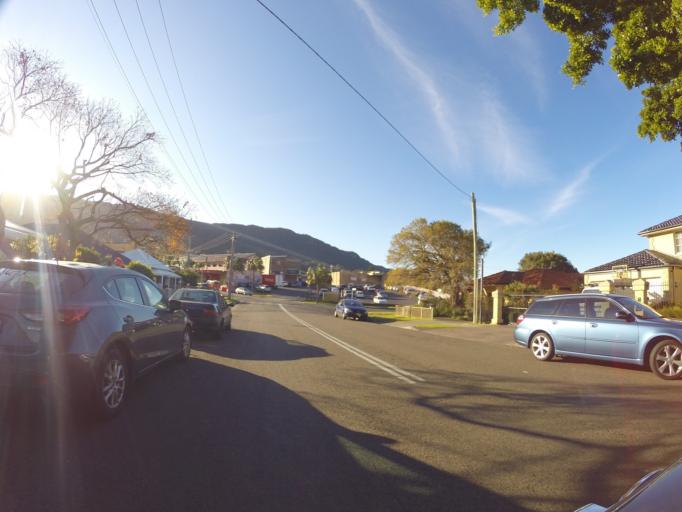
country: AU
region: New South Wales
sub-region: Wollongong
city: Bulli
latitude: -34.3163
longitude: 150.9232
